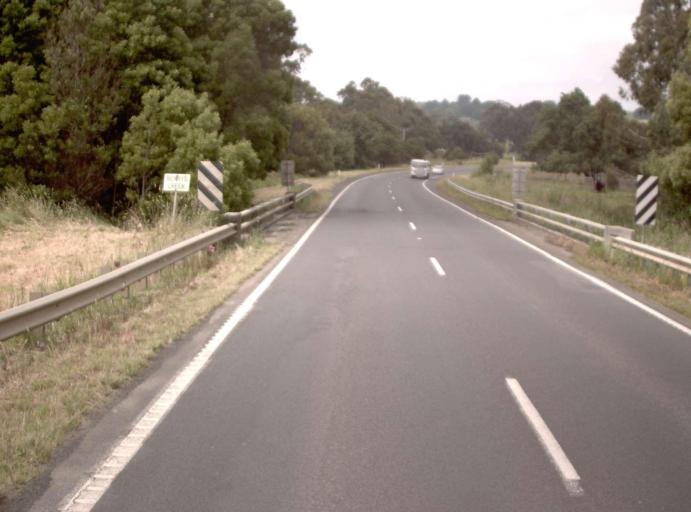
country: AU
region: Victoria
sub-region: Baw Baw
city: Warragul
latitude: -38.4031
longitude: 146.0712
